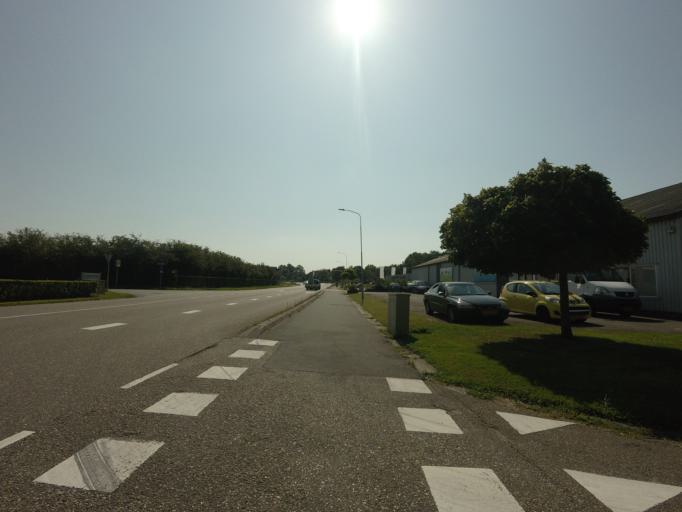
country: NL
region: Groningen
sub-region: Gemeente Zuidhorn
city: Grijpskerk
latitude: 53.2666
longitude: 6.3067
